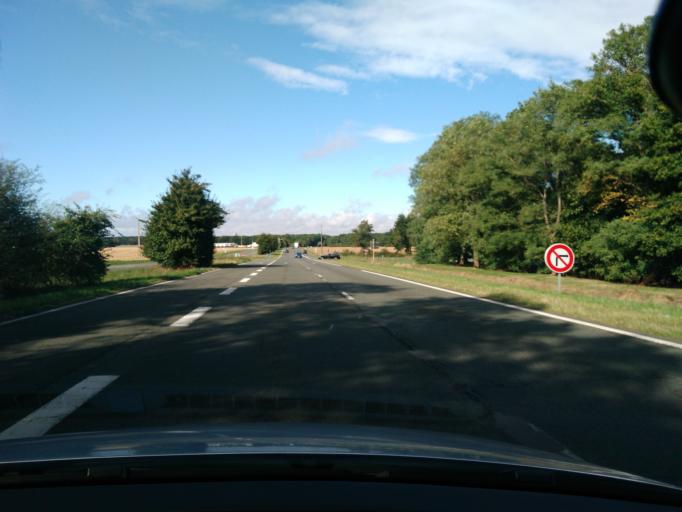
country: FR
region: Haute-Normandie
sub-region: Departement de l'Eure
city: Saint-Germain-sur-Avre
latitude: 48.7484
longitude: 1.2707
